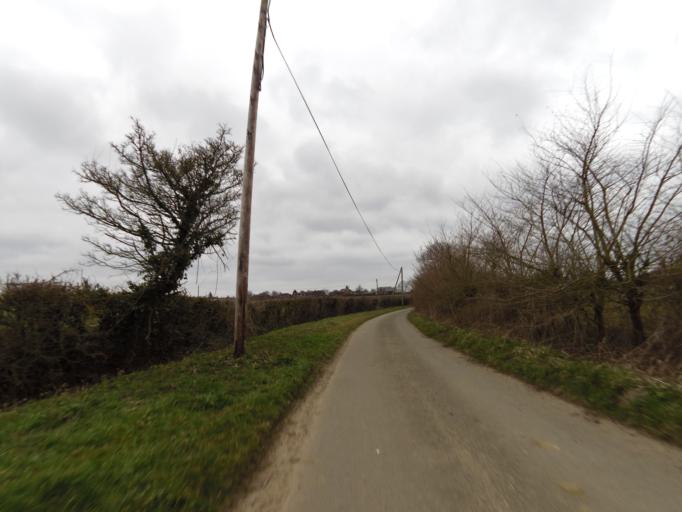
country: GB
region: England
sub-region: Suffolk
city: Ipswich
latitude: 52.1174
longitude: 1.1597
